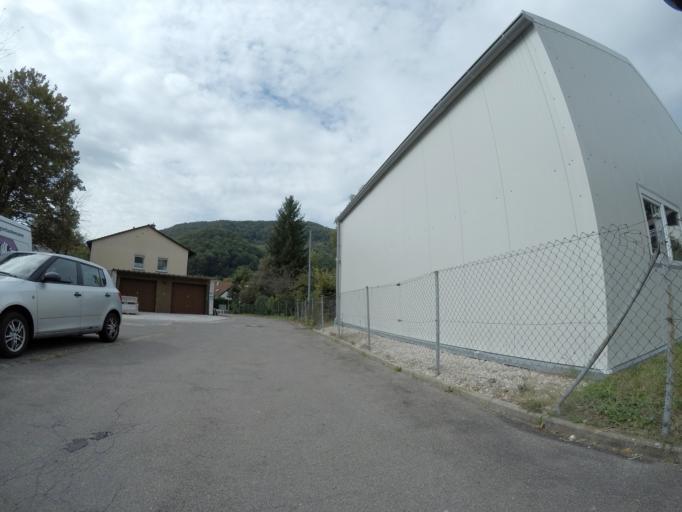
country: DE
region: Baden-Wuerttemberg
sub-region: Tuebingen Region
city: Pfullingen
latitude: 48.4283
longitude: 9.2581
